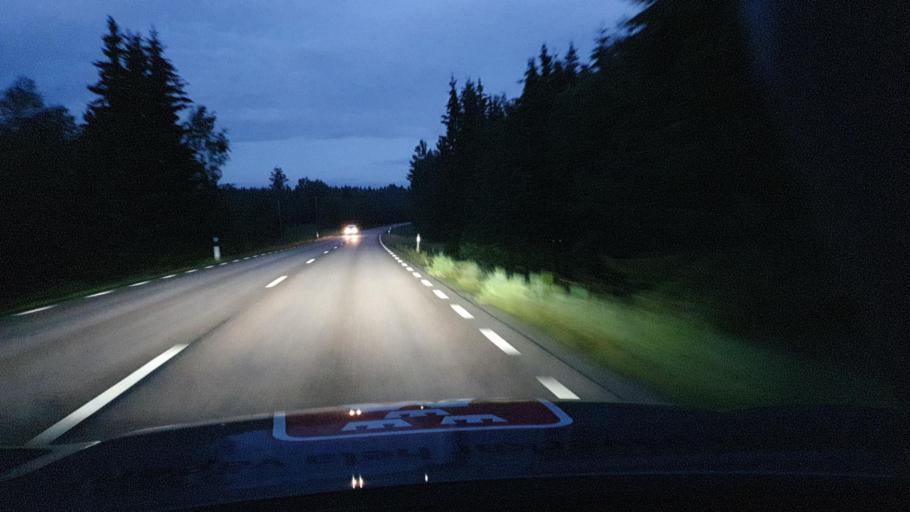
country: SE
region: Vaermland
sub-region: Storfors Kommun
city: Storfors
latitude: 59.4514
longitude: 14.3862
